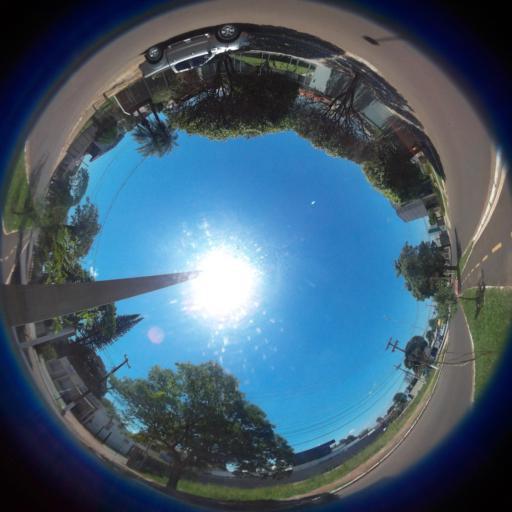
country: BR
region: Mato Grosso do Sul
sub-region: Ponta Pora
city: Ponta Pora
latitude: -22.5372
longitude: -55.7217
